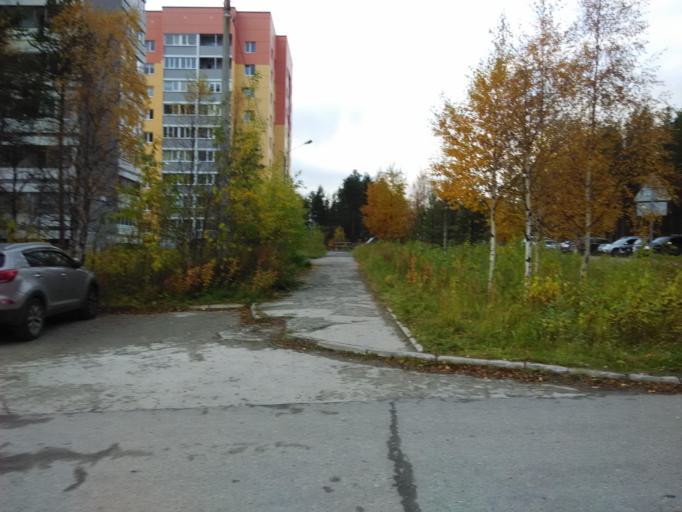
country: RU
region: Murmansk
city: Polyarnyye Zori
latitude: 67.3694
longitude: 32.4783
